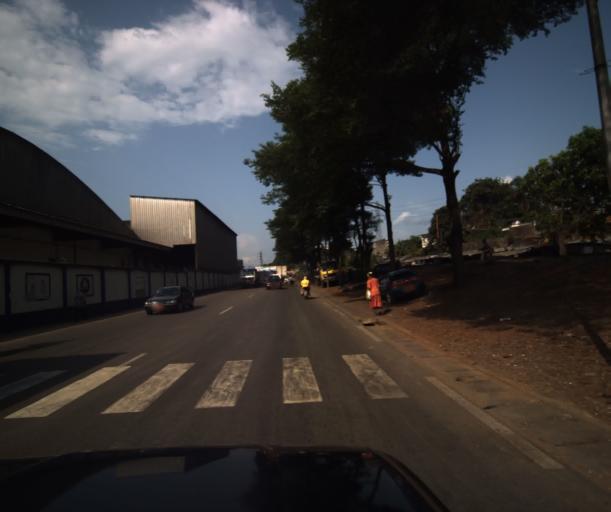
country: CM
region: Littoral
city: Douala
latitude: 4.0638
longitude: 9.7034
